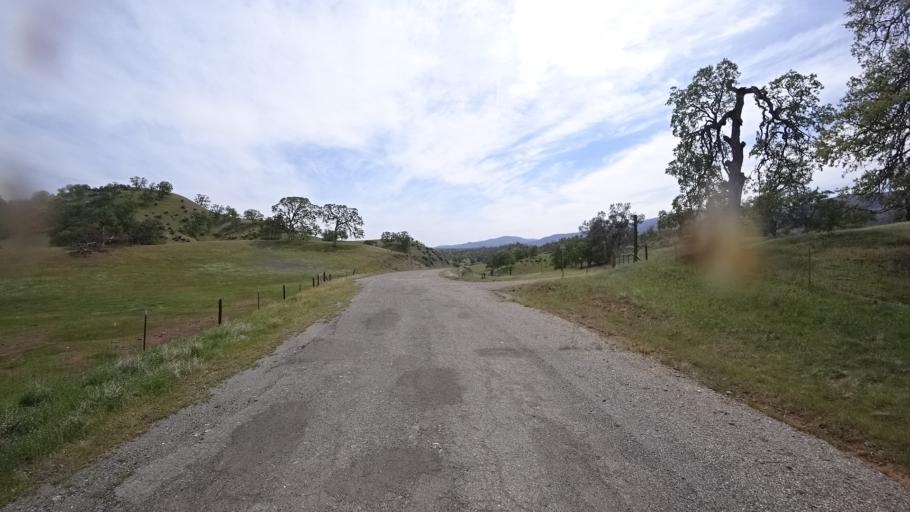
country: US
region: California
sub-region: Glenn County
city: Willows
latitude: 39.6214
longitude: -122.5923
